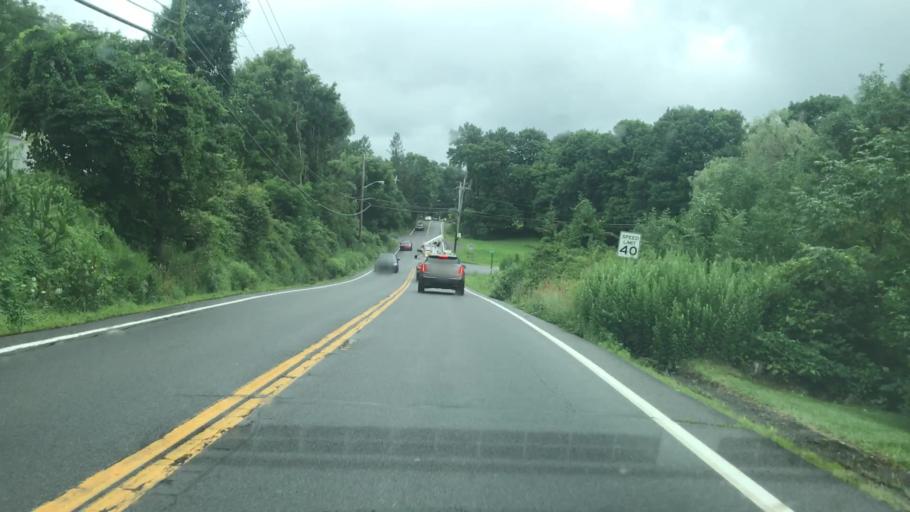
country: US
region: New York
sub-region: Westchester County
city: Jefferson Valley-Yorktown
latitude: 41.3486
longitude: -73.7823
